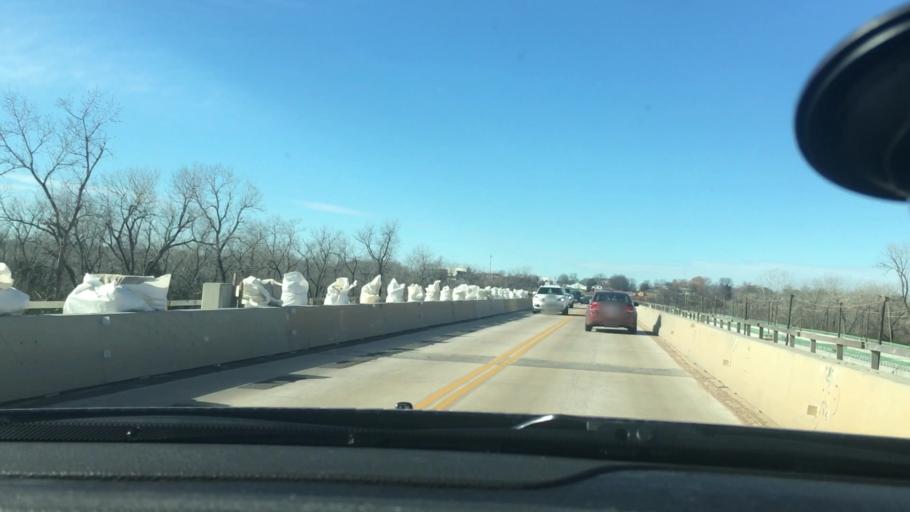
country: US
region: Oklahoma
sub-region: McClain County
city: Purcell
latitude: 35.0144
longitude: -97.3493
